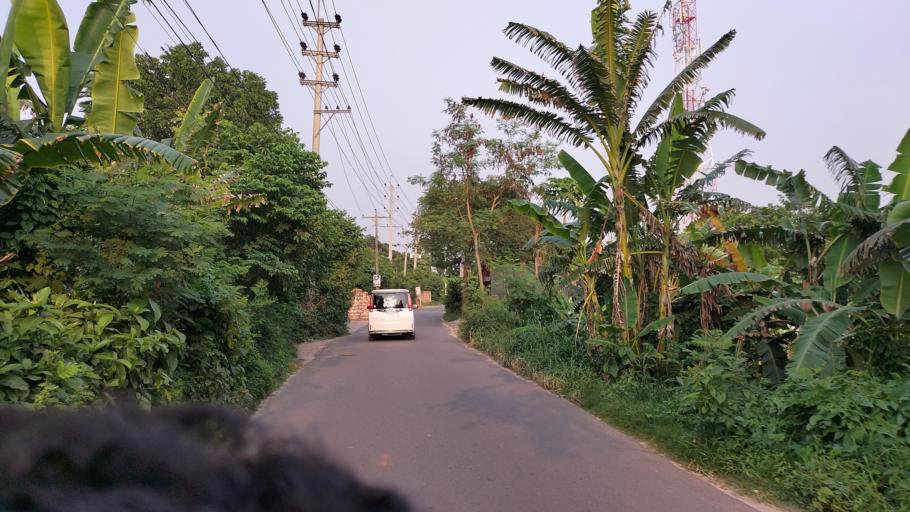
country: BD
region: Dhaka
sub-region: Dhaka
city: Dhaka
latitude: 23.6534
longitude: 90.3467
